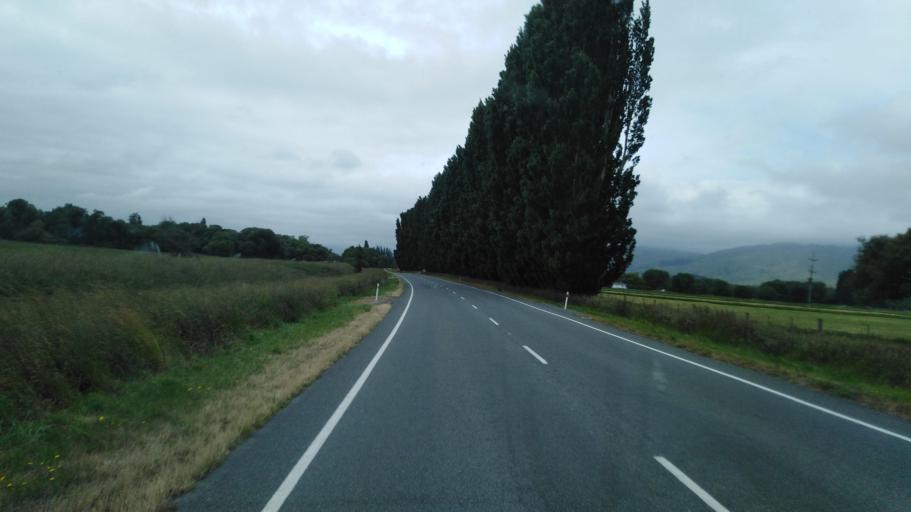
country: NZ
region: Canterbury
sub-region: Kaikoura District
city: Kaikoura
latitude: -42.7335
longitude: 173.2735
